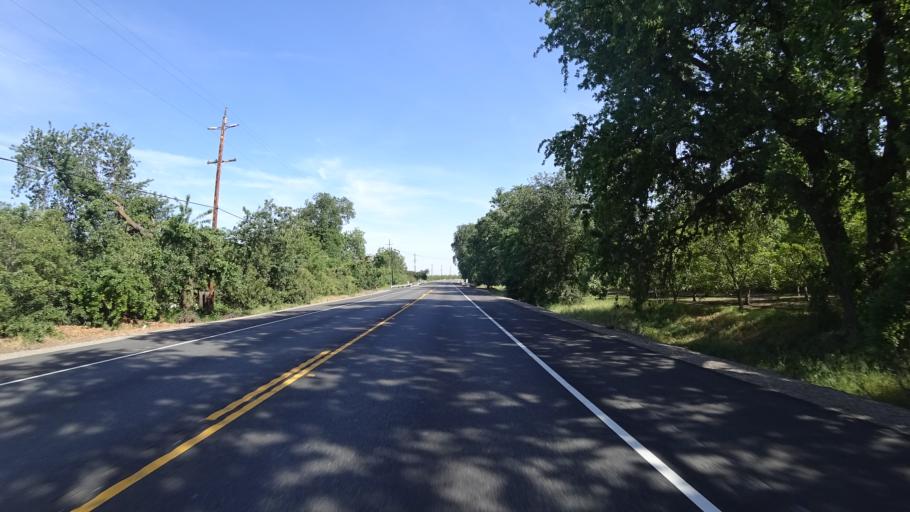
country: US
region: California
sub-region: Glenn County
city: Hamilton City
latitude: 39.8814
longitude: -121.9738
